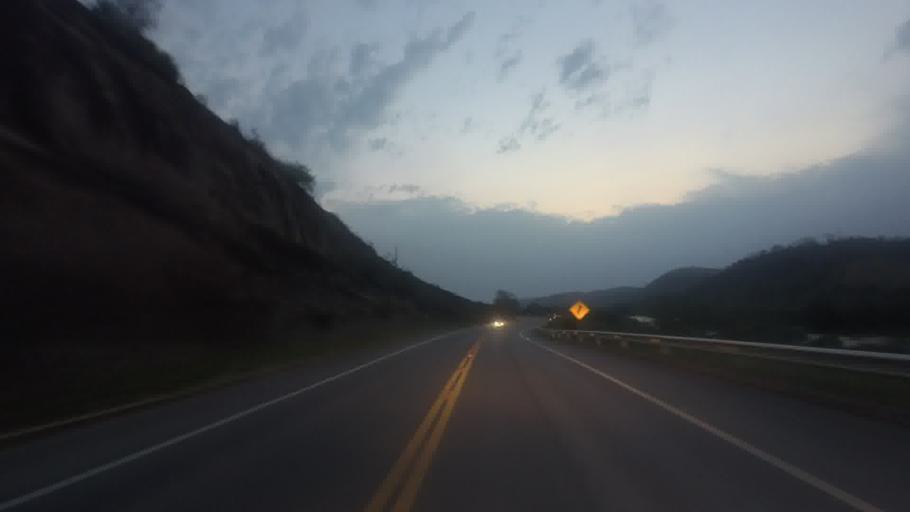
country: BR
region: Minas Gerais
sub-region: Alem Paraiba
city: Alem Paraiba
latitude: -21.9114
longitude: -42.7437
